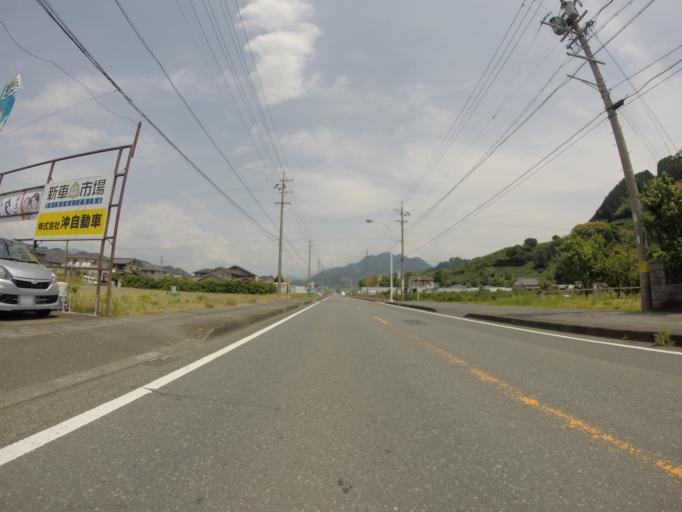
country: JP
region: Shizuoka
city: Shizuoka-shi
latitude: 35.0209
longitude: 138.3757
